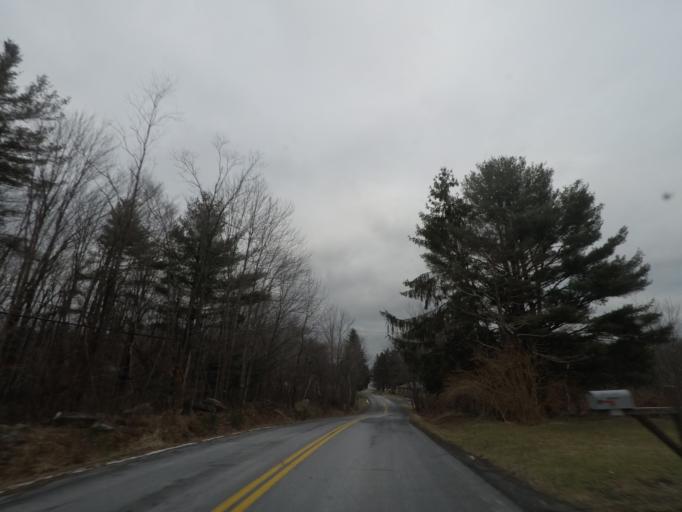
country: US
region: New York
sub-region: Rensselaer County
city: Poestenkill
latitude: 42.7671
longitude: -73.4752
